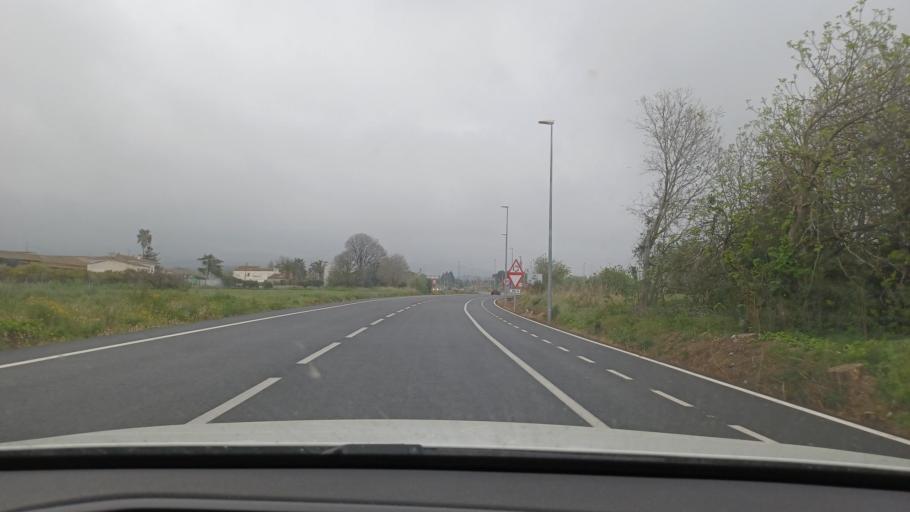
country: ES
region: Catalonia
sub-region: Provincia de Tarragona
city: Tortosa
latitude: 40.8070
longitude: 0.5036
